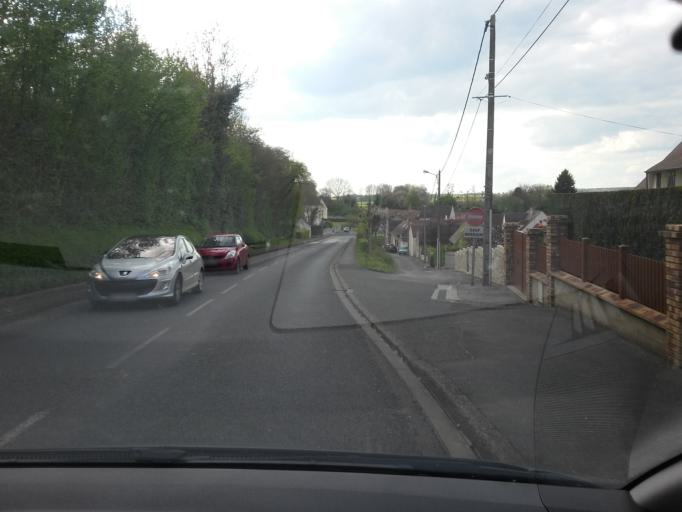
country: FR
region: Picardie
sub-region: Departement de l'Oise
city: Grandfresnoy
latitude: 49.3724
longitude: 2.6516
